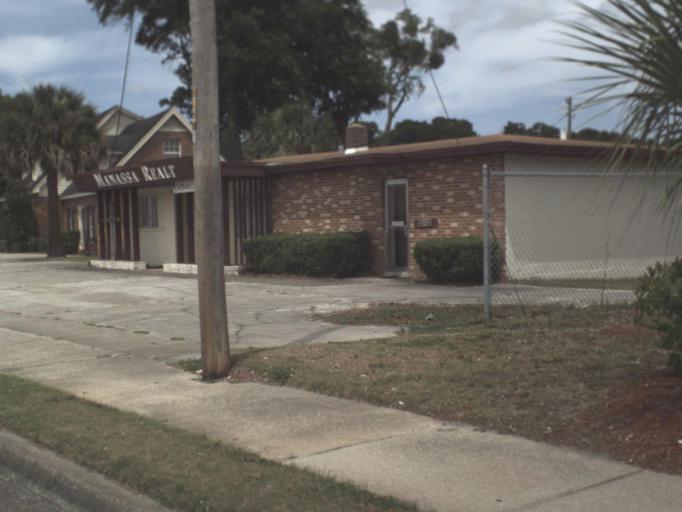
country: US
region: Florida
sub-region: Clay County
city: Bellair-Meadowbrook Terrace
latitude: 30.2674
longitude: -81.7374
